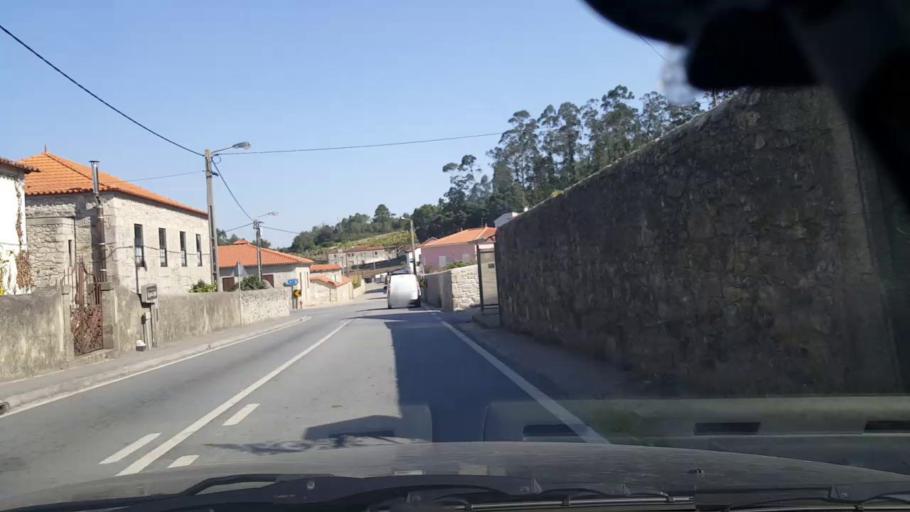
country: PT
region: Porto
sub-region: Vila do Conde
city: Arvore
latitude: 41.3744
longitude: -8.6704
